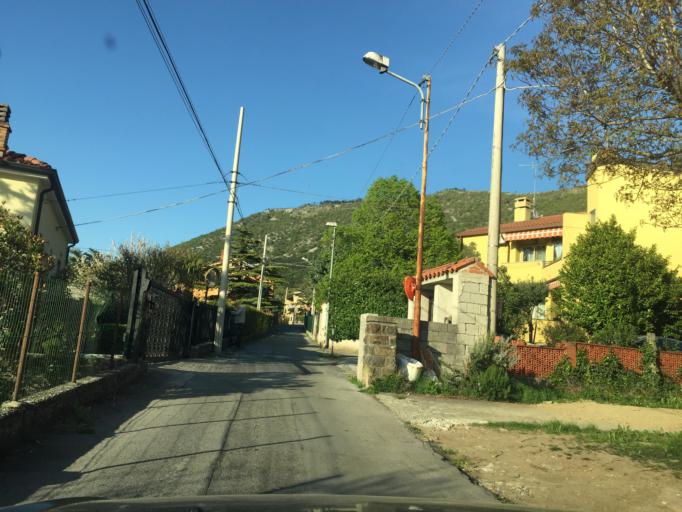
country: IT
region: Friuli Venezia Giulia
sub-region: Provincia di Trieste
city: Dolina
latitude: 45.6020
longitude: 13.8542
